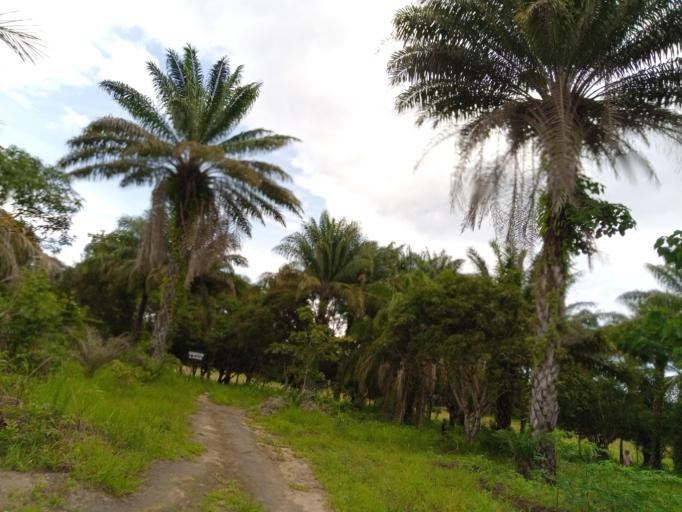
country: SL
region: Northern Province
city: Masoyila
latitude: 8.5696
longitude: -13.1644
